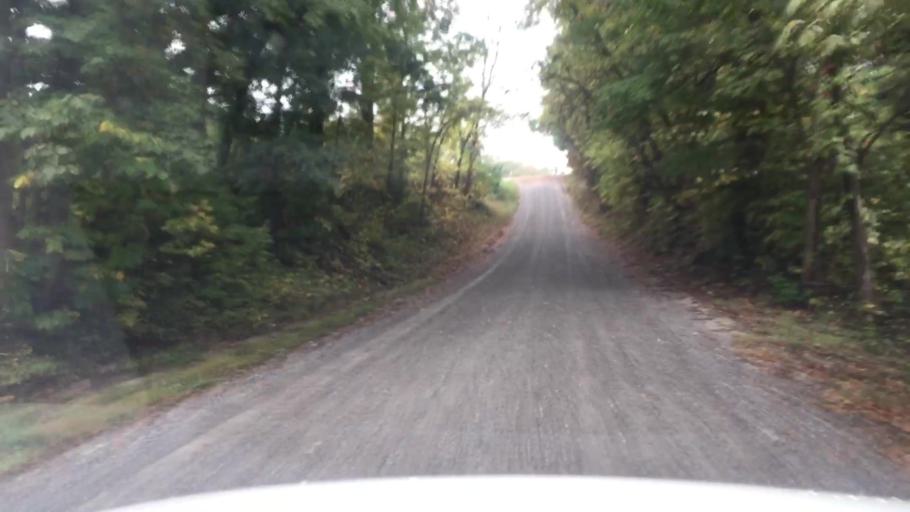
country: US
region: Missouri
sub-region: Boone County
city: Columbia
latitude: 38.8878
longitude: -92.4196
